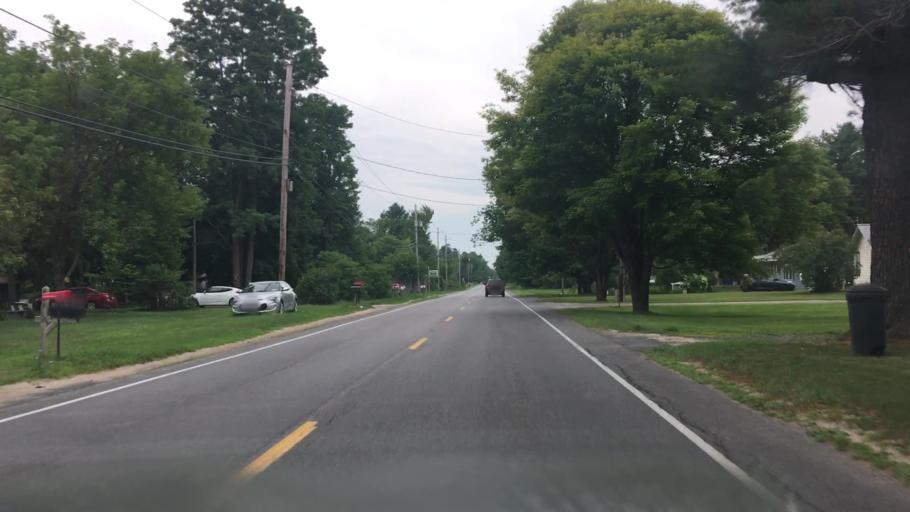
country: US
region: New York
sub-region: Clinton County
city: Plattsburgh West
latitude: 44.6586
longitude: -73.5101
